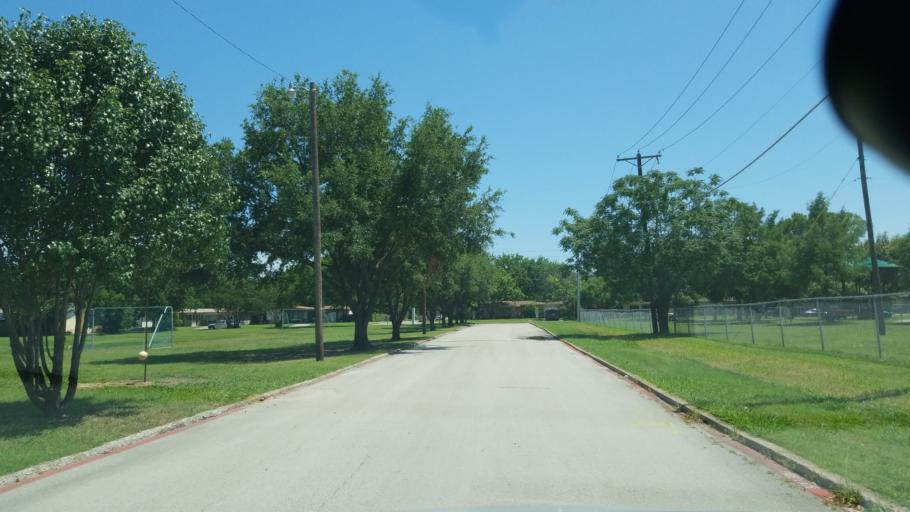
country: US
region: Texas
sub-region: Dallas County
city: Irving
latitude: 32.8300
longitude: -96.9677
